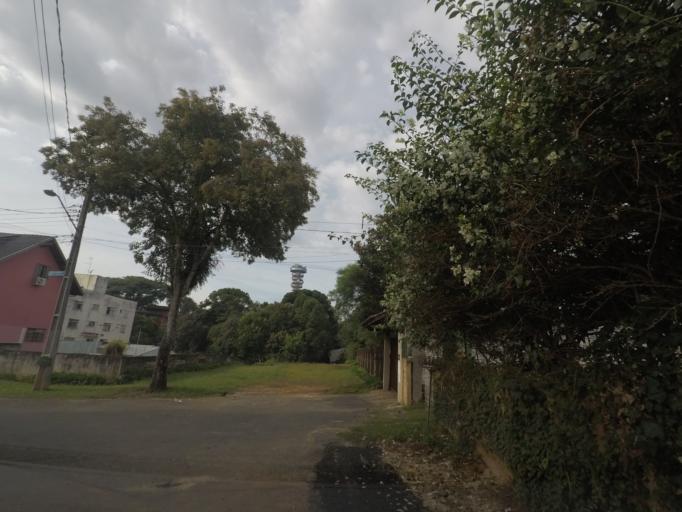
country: BR
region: Parana
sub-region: Curitiba
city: Curitiba
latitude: -25.4204
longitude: -49.2967
